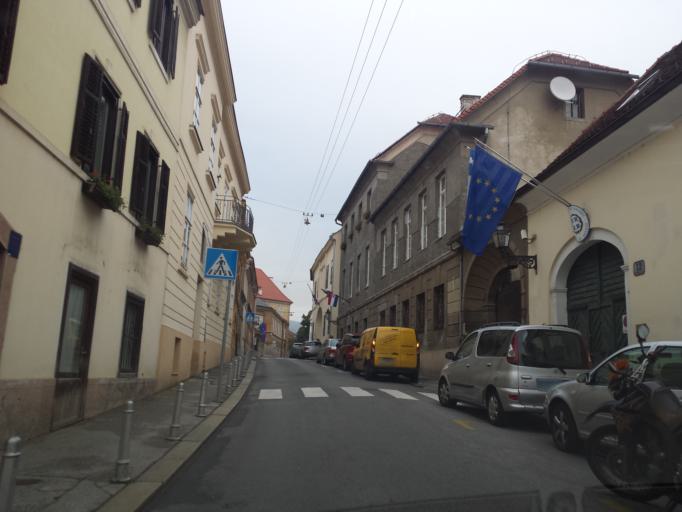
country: HR
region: Grad Zagreb
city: Zagreb
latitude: 45.8172
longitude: 15.9748
